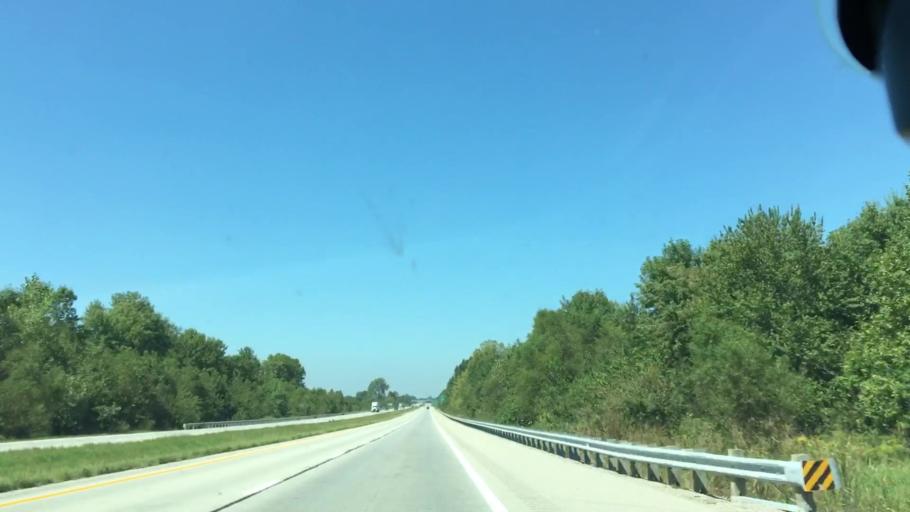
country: US
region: Kentucky
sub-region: Henderson County
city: Henderson
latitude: 37.7794
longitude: -87.5435
